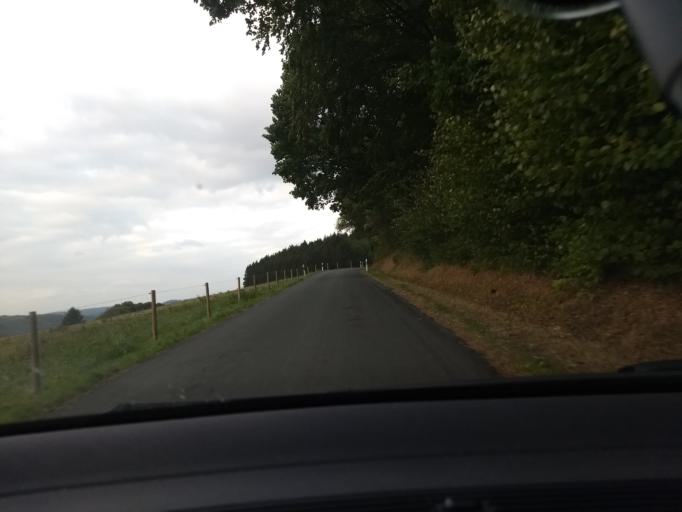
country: DE
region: North Rhine-Westphalia
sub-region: Regierungsbezirk Arnsberg
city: Arnsberg
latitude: 51.3361
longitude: 8.1102
